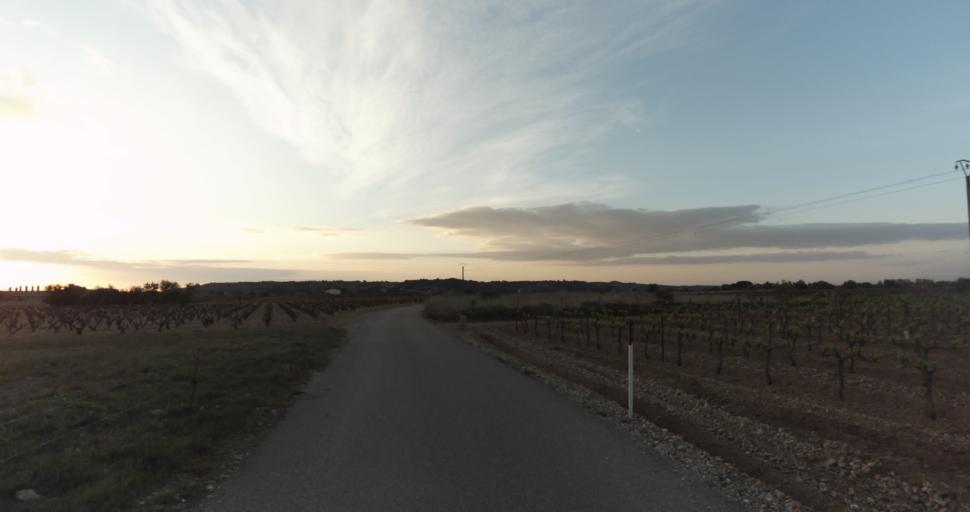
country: FR
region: Languedoc-Roussillon
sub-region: Departement de l'Aude
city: Leucate
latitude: 42.9364
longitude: 3.0010
